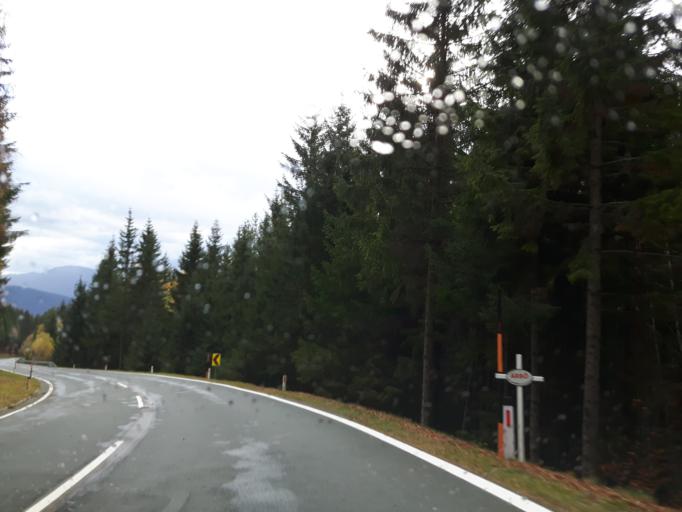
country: AT
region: Carinthia
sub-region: Politischer Bezirk Wolfsberg
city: Lavamund
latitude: 46.6483
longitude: 14.9832
